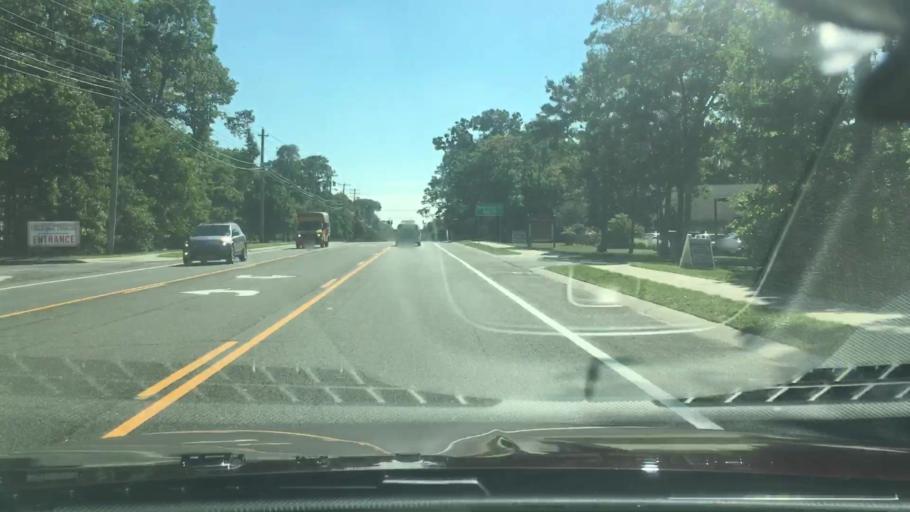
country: US
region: New York
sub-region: Suffolk County
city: Port Jefferson Station
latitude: 40.9032
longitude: -73.0247
